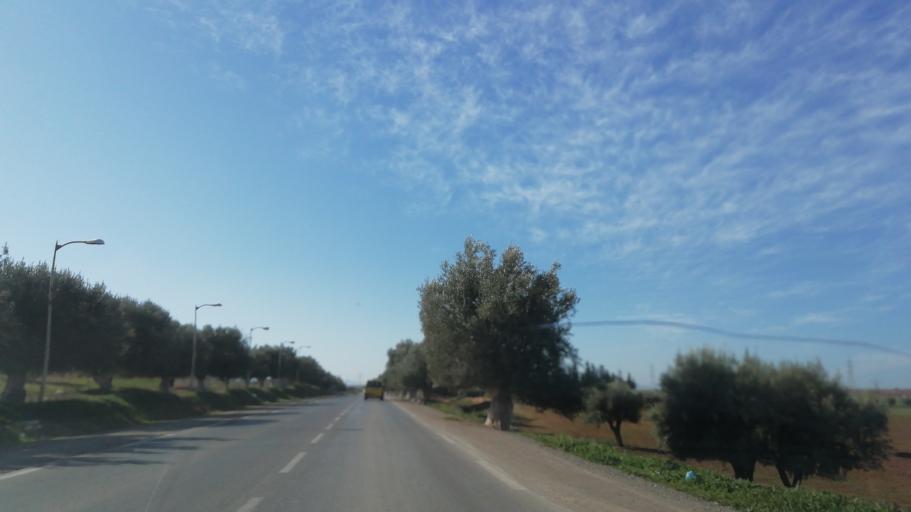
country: DZ
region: Tlemcen
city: Ouled Mimoun
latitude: 35.0240
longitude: -0.8961
